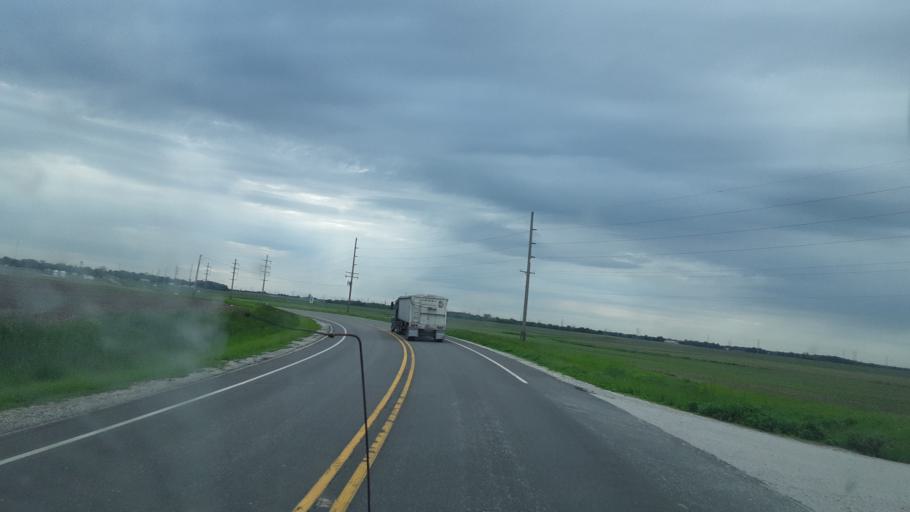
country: US
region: Illinois
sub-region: Fulton County
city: Astoria
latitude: 40.3522
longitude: -90.3522
